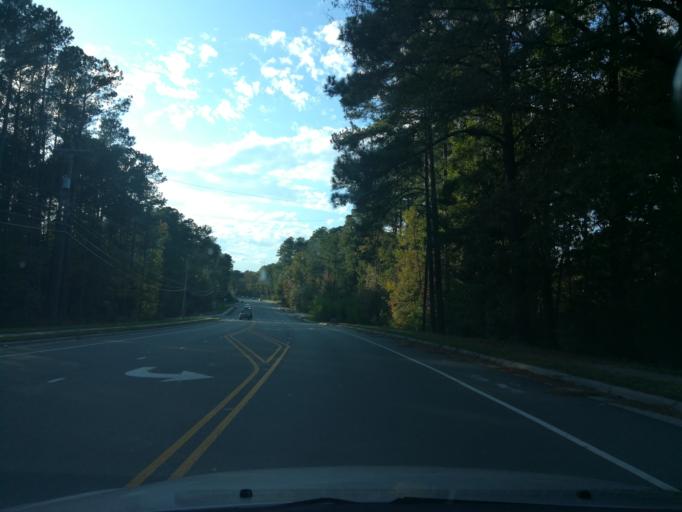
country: US
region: North Carolina
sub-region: Orange County
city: Chapel Hill
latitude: 35.9638
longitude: -79.0406
